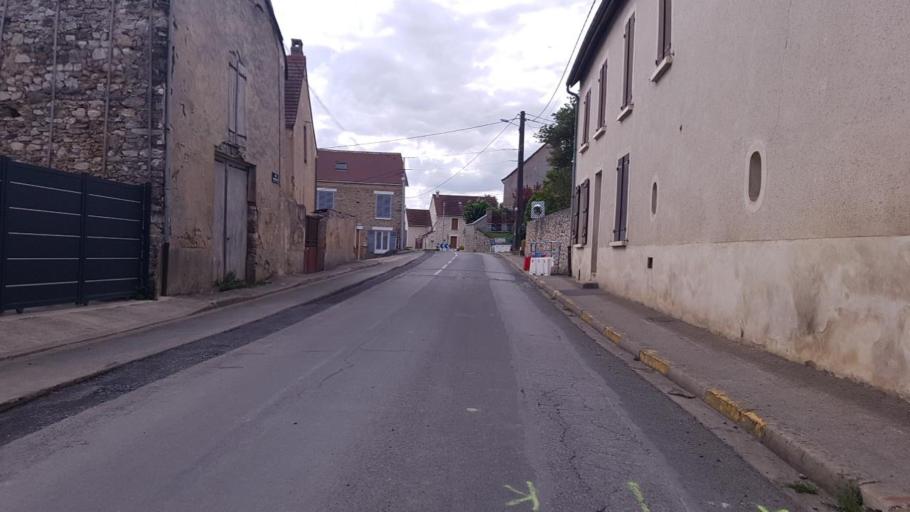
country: FR
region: Picardie
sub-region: Departement de l'Aisne
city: Crezancy
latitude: 49.0757
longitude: 3.5025
